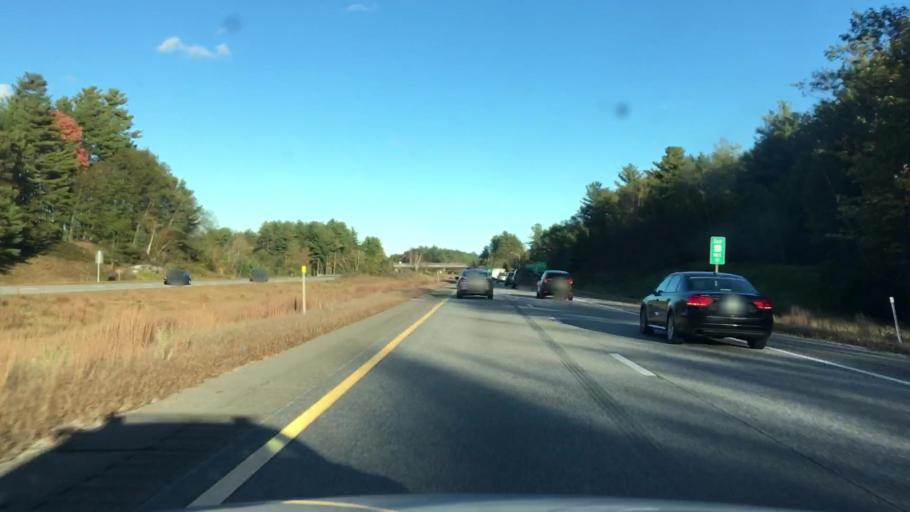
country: US
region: New Hampshire
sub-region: Rockingham County
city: Raymond
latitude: 43.0232
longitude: -71.2049
